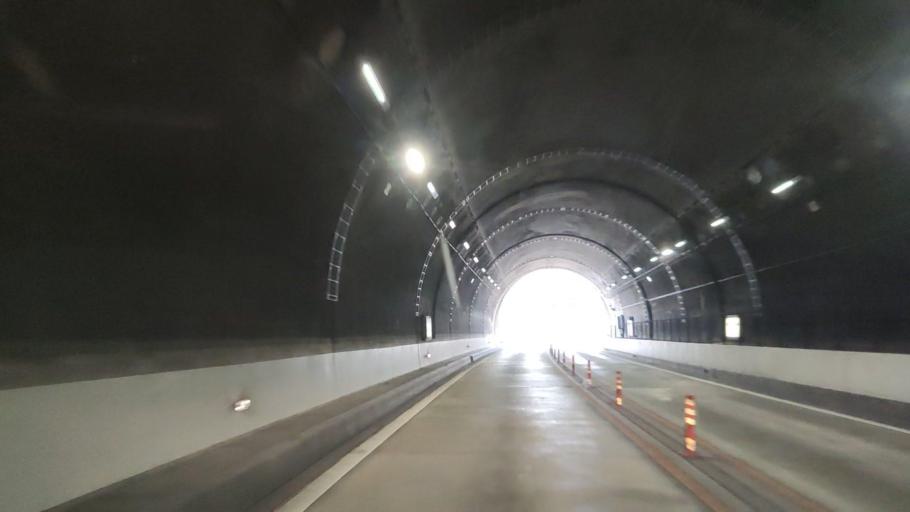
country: JP
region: Hiroshima
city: Innoshima
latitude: 34.1874
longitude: 133.0692
